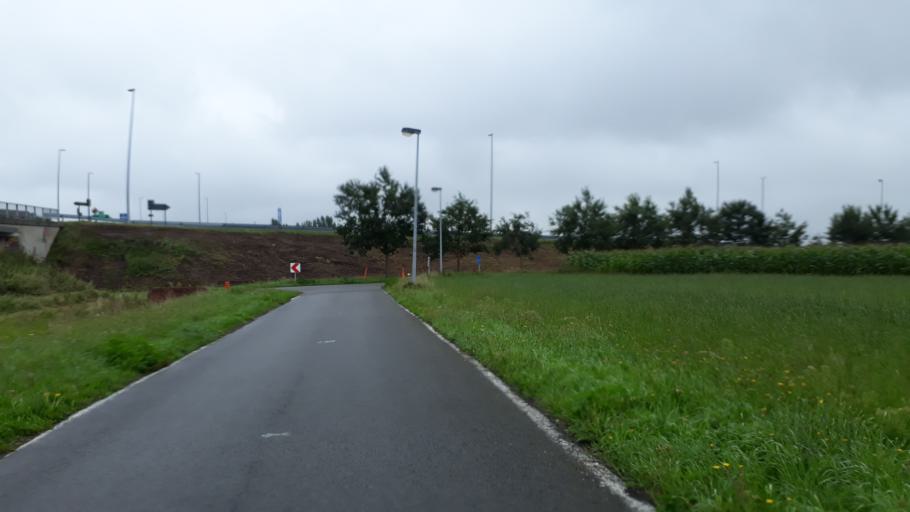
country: BE
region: Flanders
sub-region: Provincie West-Vlaanderen
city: Lichtervelde
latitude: 51.0786
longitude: 3.1512
